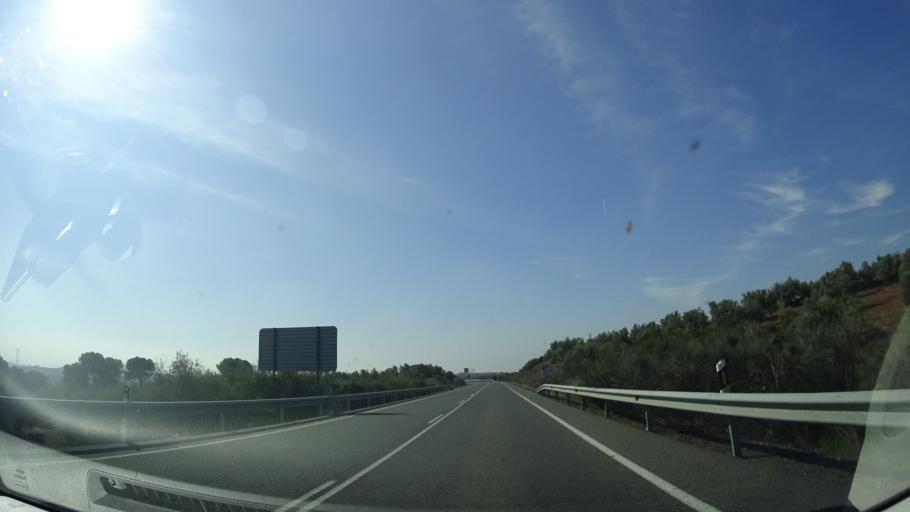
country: ES
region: Andalusia
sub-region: Province of Cordoba
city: Montoro
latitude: 38.0623
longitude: -4.3780
